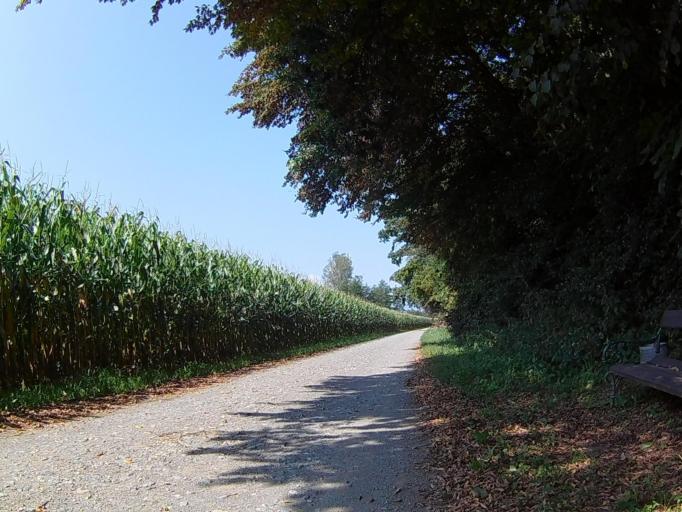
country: AT
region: Styria
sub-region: Politischer Bezirk Leibnitz
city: Oberhaag
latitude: 46.6880
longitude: 15.3492
